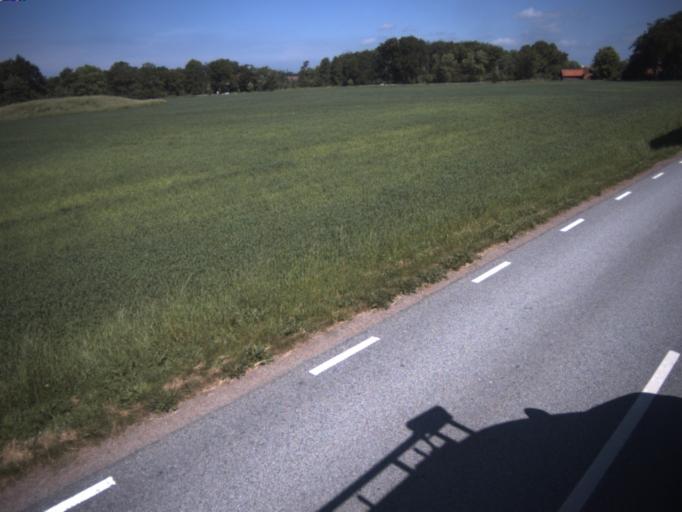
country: DK
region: Capital Region
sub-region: Helsingor Kommune
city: Helsingor
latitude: 56.1047
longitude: 12.6387
